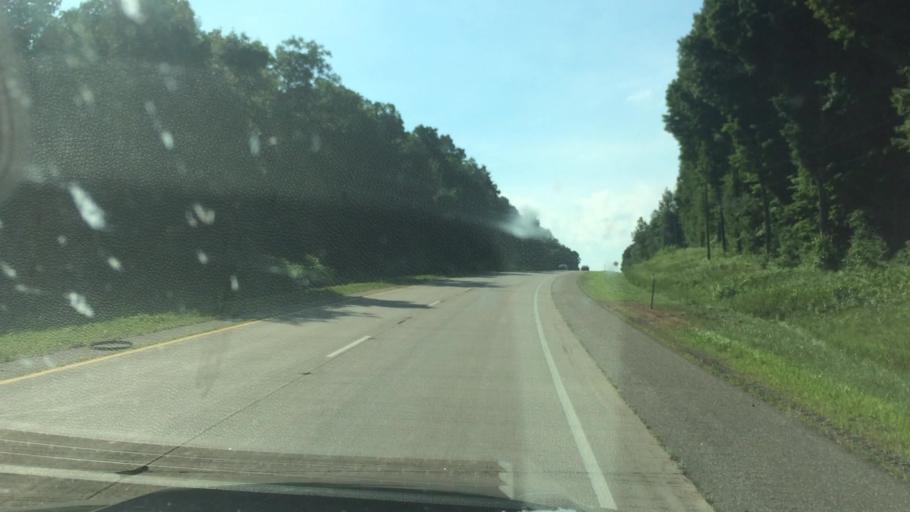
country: US
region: Wisconsin
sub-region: Shawano County
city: Wittenberg
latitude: 44.8231
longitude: -89.0596
